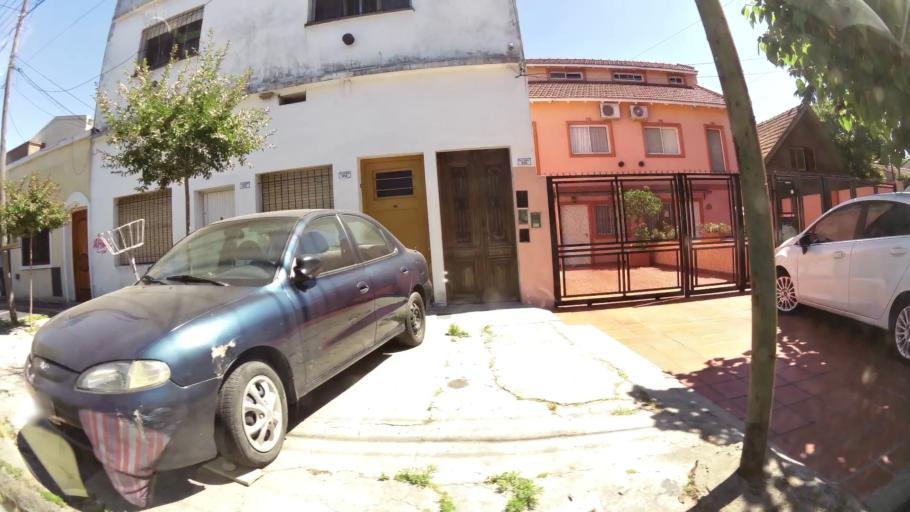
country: AR
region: Buenos Aires
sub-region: Partido de San Isidro
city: San Isidro
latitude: -34.5055
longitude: -58.5761
